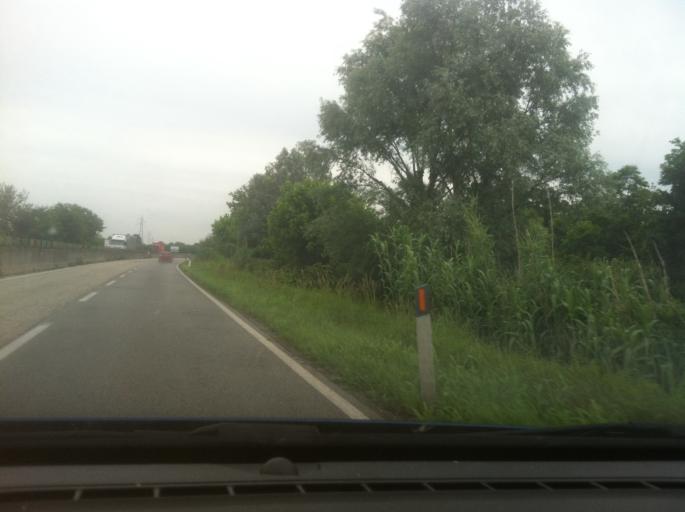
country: IT
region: Piedmont
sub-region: Provincia di Torino
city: Settimo Torinese
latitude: 45.1286
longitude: 7.7738
